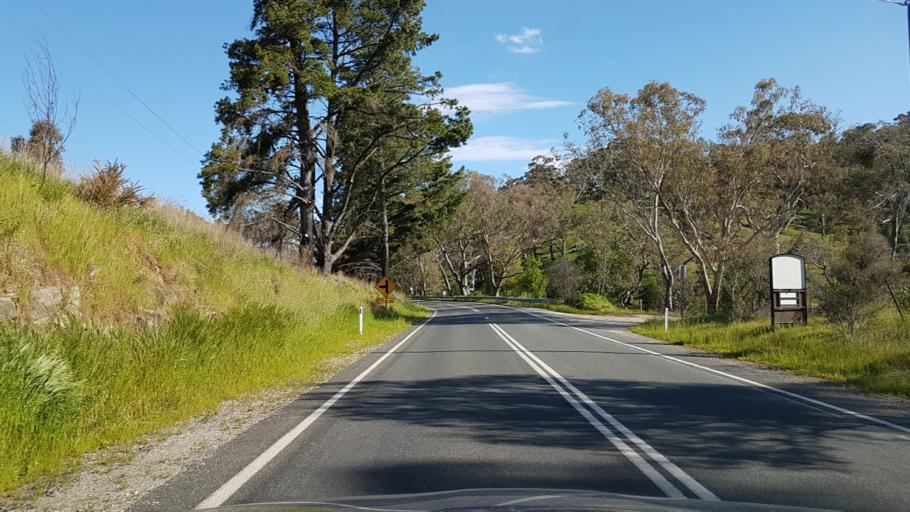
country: AU
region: South Australia
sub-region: Adelaide Hills
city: Gumeracha
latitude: -34.8312
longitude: 138.8910
